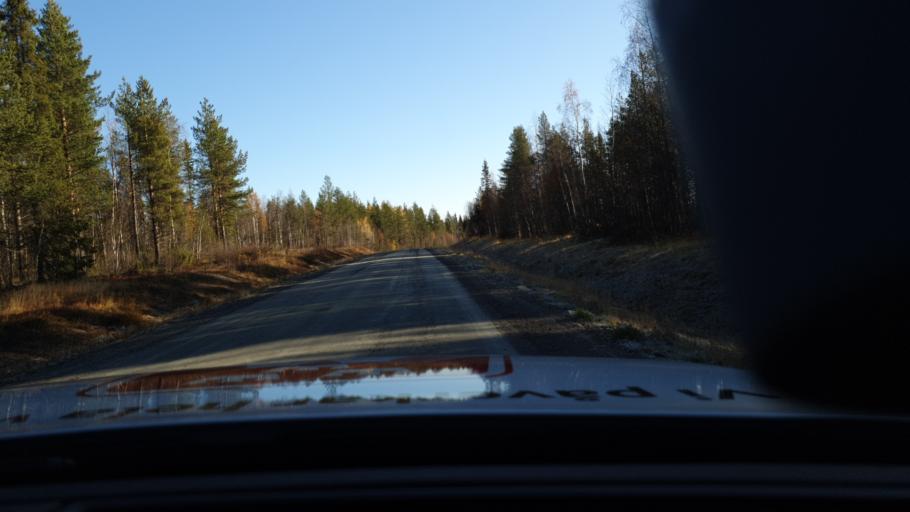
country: SE
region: Norrbotten
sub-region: Gallivare Kommun
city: Malmberget
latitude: 67.4004
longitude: 21.8800
